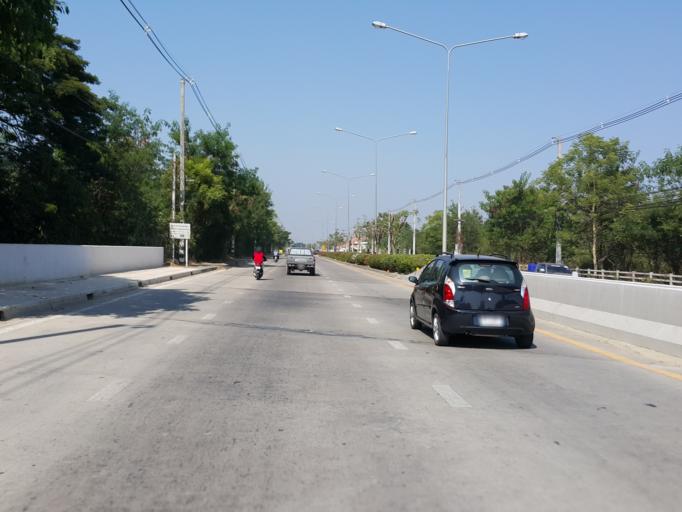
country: TH
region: Chiang Mai
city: Chiang Mai
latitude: 18.7889
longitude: 99.0399
